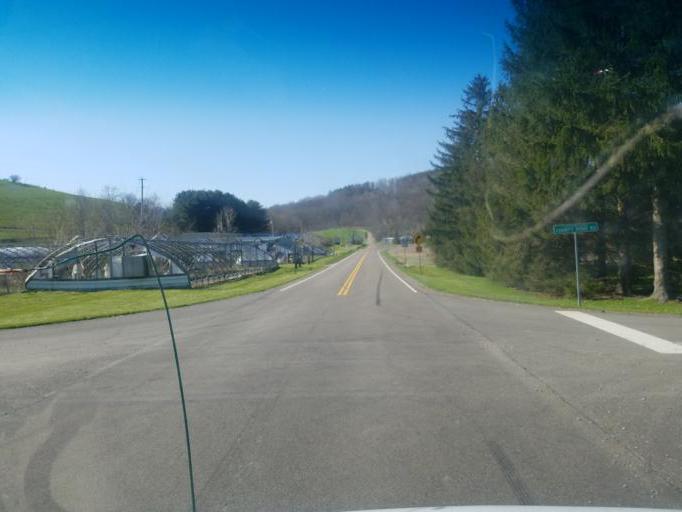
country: US
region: Ohio
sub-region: Knox County
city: Oak Hill
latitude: 40.3197
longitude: -82.0796
